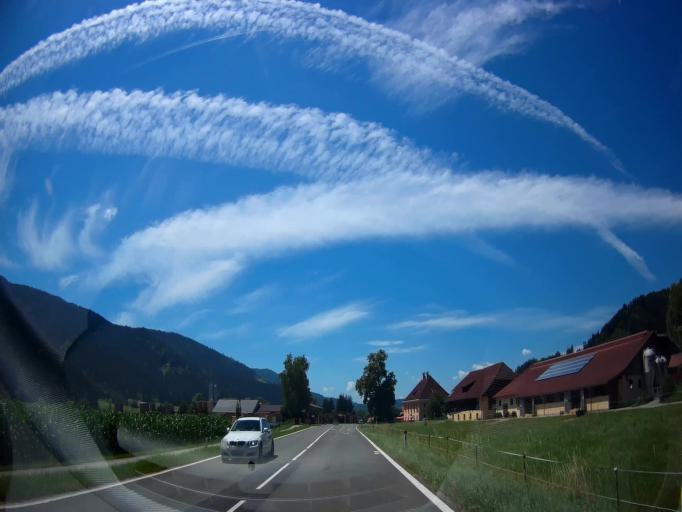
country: AT
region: Carinthia
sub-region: Politischer Bezirk Sankt Veit an der Glan
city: Micheldorf
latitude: 46.9026
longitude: 14.3883
